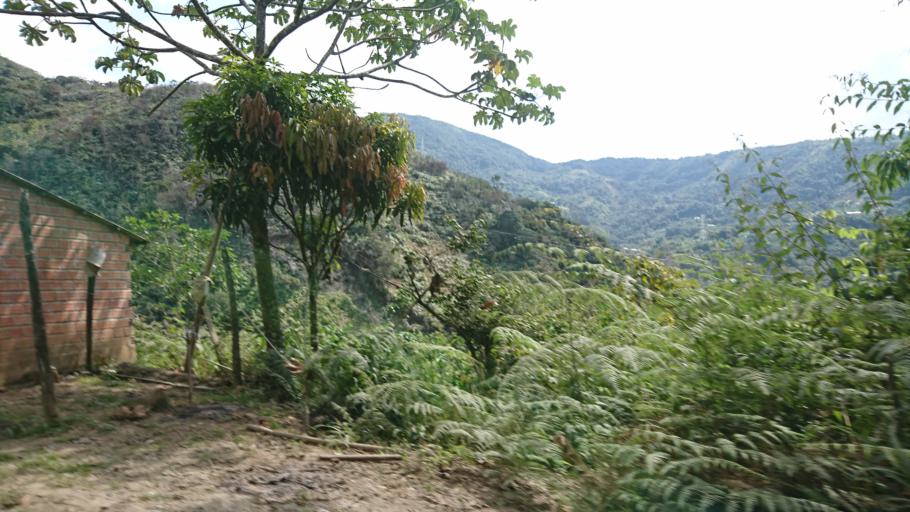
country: BO
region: La Paz
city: Coroico
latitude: -16.0844
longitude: -67.7880
